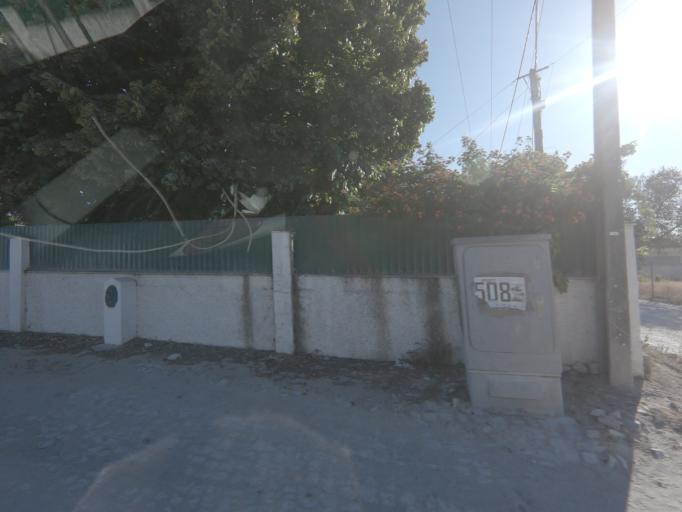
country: PT
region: Setubal
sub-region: Palmela
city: Palmela
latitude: 38.5883
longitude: -8.9184
